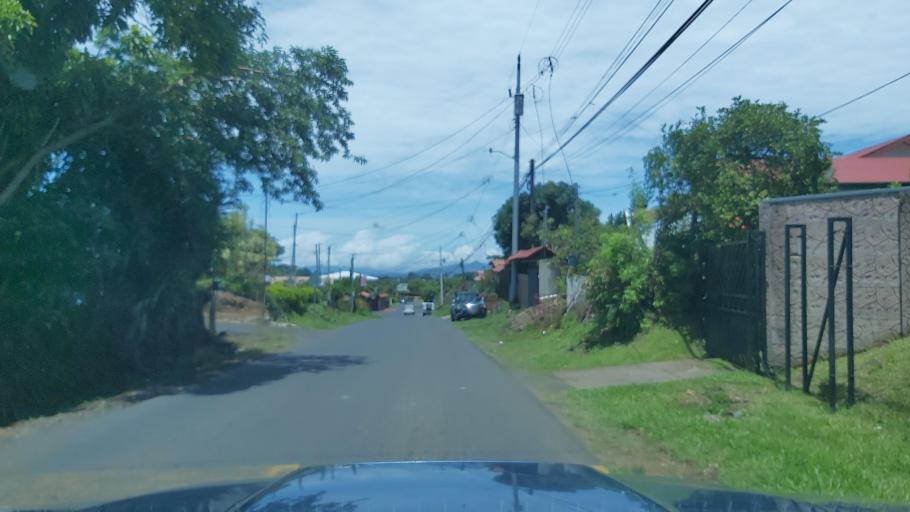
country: CR
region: Alajuela
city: San Juan
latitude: 10.0900
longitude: -84.3417
